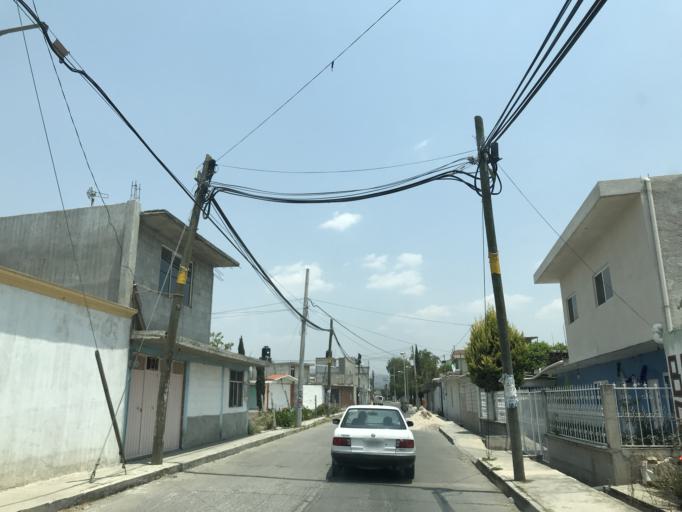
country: MX
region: Tlaxcala
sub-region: Ixtacuixtla de Mariano Matamoros
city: Santa Justina Ecatepec
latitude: 19.3088
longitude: -98.3720
